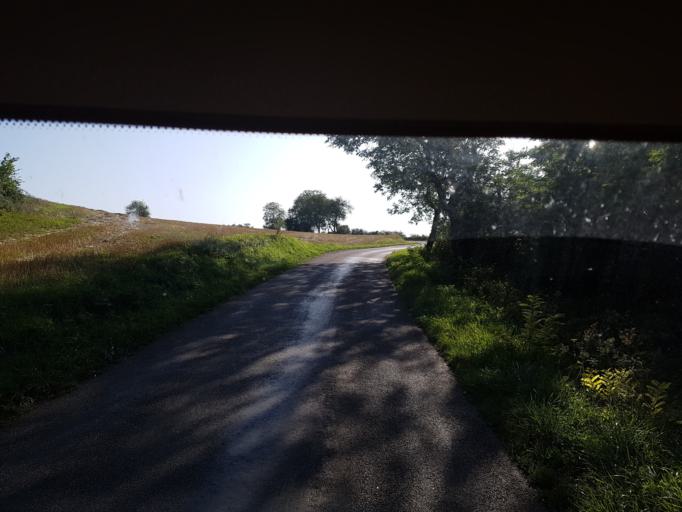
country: FR
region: Rhone-Alpes
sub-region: Departement de l'Ain
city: Villereversure
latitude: 46.1458
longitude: 5.4122
